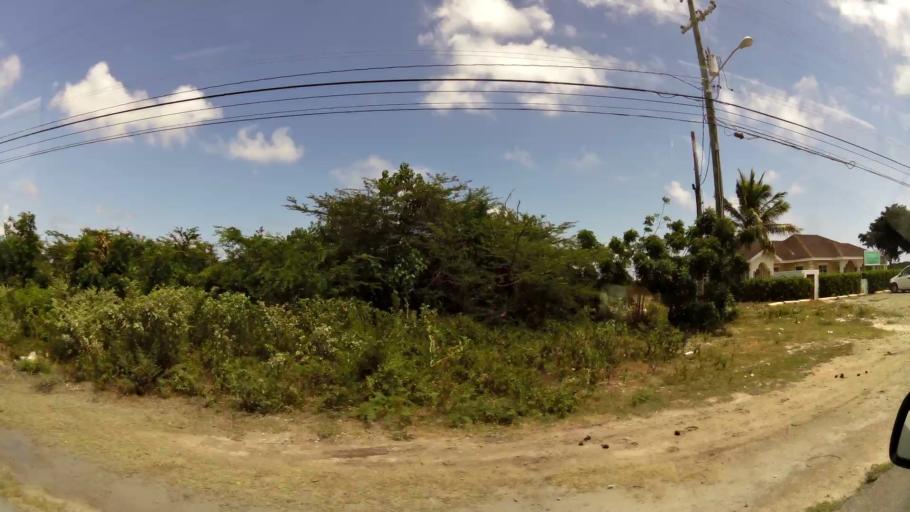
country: TC
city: Cockburn Town
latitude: 21.4387
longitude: -71.1472
